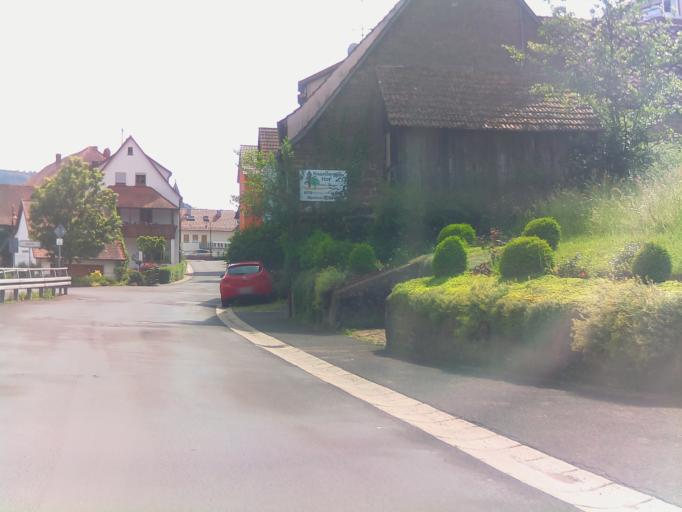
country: DE
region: Bavaria
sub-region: Regierungsbezirk Unterfranken
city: Hasloch
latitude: 49.7940
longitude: 9.4928
